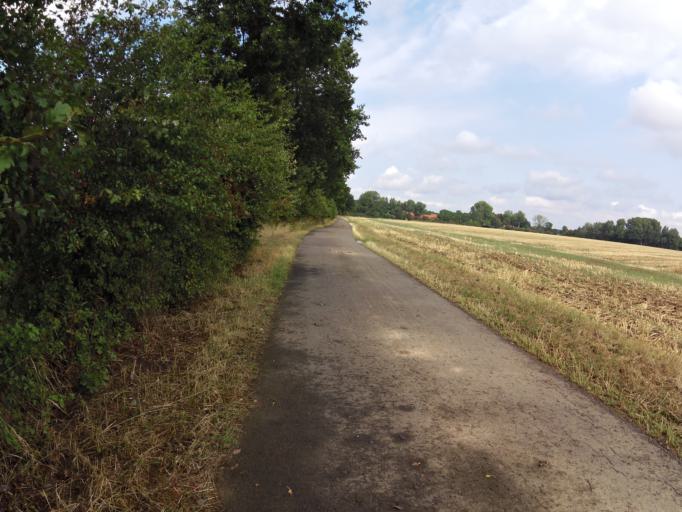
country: DE
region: Lower Saxony
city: Schweringen
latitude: 52.7664
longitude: 9.1753
